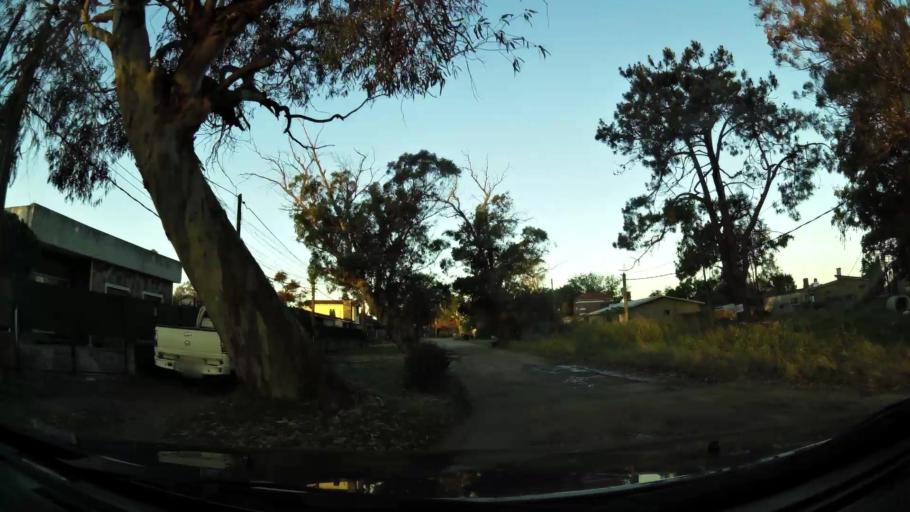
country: UY
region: Canelones
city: Barra de Carrasco
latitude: -34.8485
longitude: -55.9806
